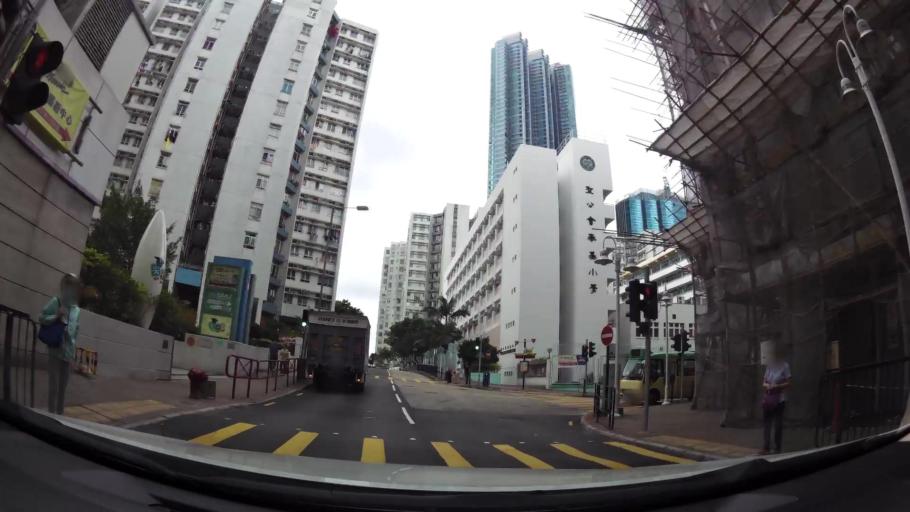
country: HK
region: Kowloon City
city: Kowloon
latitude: 22.3053
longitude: 114.1912
